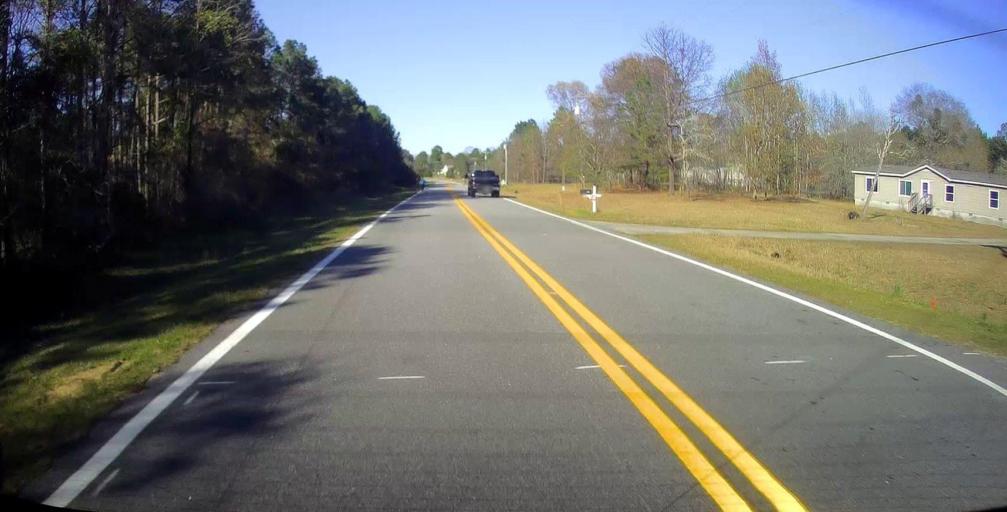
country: US
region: Georgia
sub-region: Peach County
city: Byron
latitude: 32.6816
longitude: -83.8074
